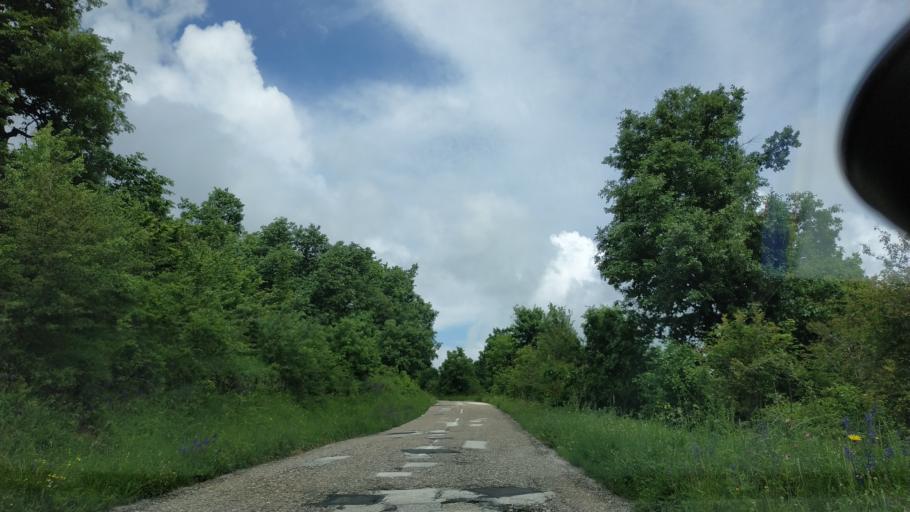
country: RS
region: Central Serbia
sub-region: Zajecarski Okrug
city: Boljevac
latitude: 43.7414
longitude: 21.9493
